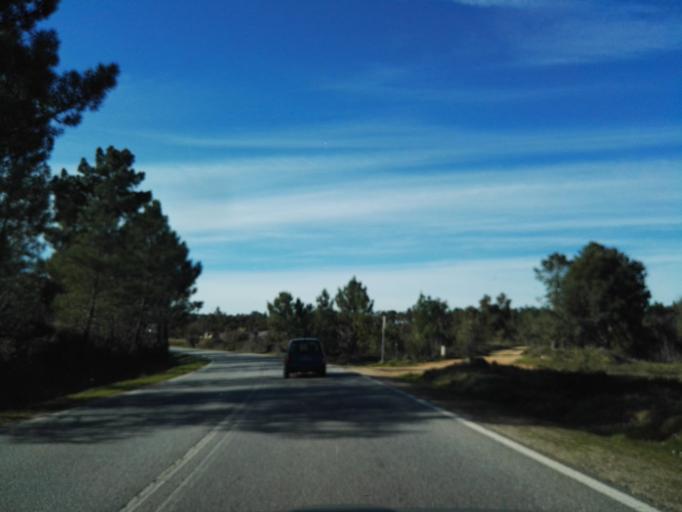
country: PT
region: Santarem
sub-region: Abrantes
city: Alferrarede
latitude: 39.4744
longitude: -8.0725
